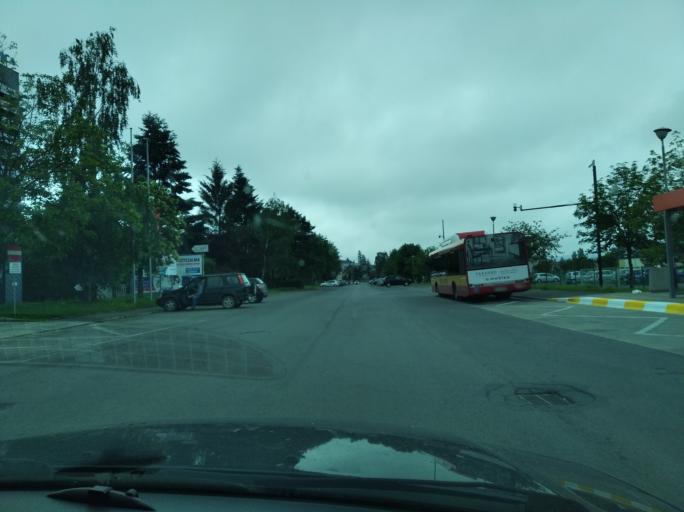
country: PL
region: Subcarpathian Voivodeship
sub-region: Rzeszow
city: Rzeszow
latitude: 50.0368
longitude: 22.0361
